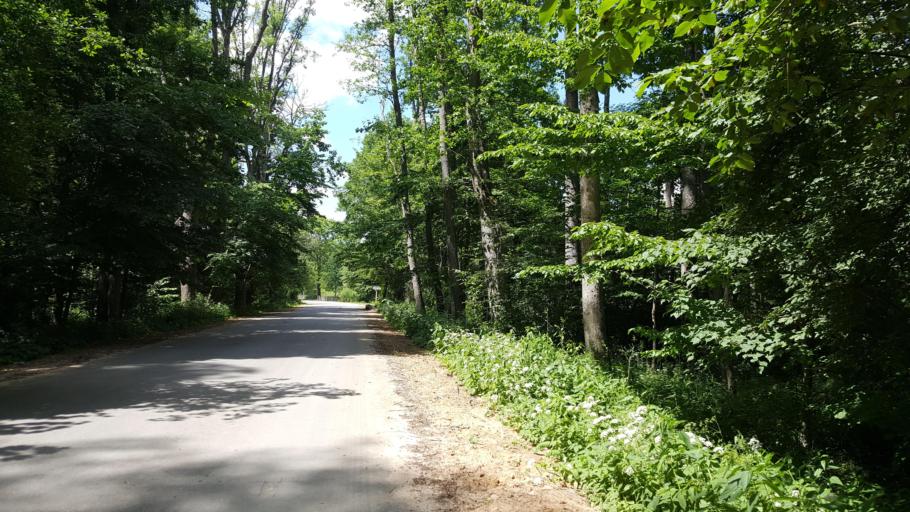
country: BY
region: Brest
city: Kamyanyuki
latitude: 52.5796
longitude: 23.7344
